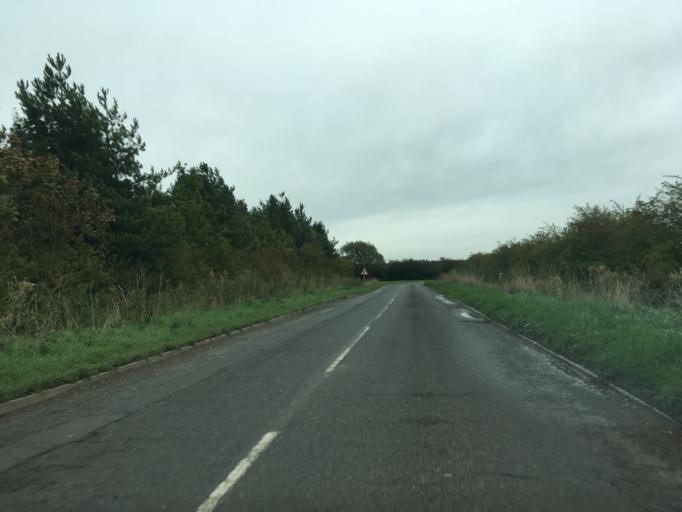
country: GB
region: England
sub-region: Nottinghamshire
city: Newark on Trent
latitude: 53.0436
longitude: -0.7985
